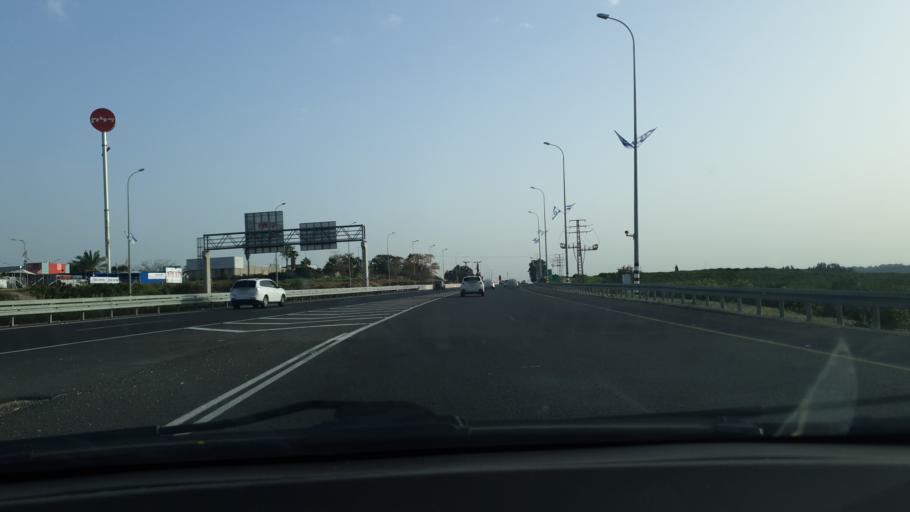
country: IL
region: Central District
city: Even Yehuda
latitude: 32.2519
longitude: 34.8899
